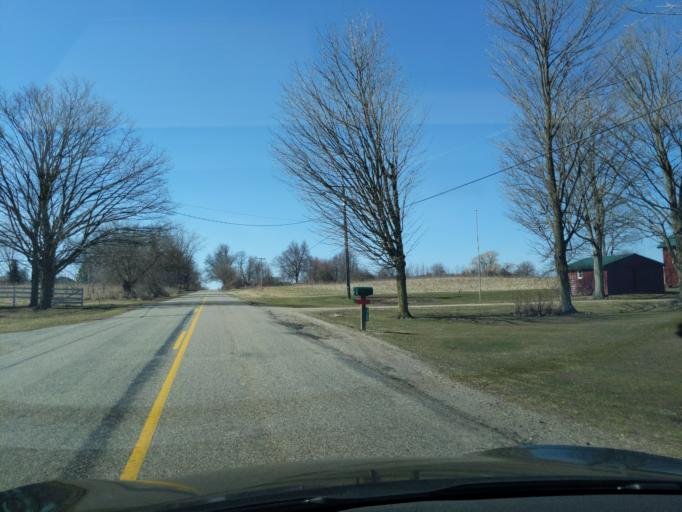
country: US
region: Michigan
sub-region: Eaton County
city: Grand Ledge
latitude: 42.7264
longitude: -84.7636
